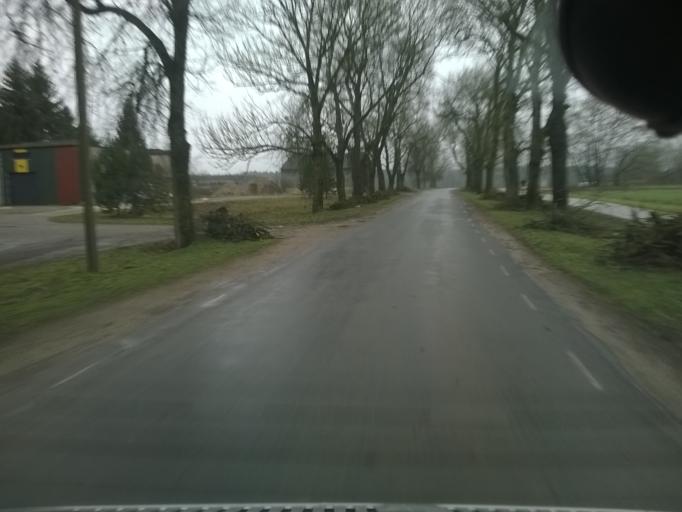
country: EE
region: Harju
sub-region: Nissi vald
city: Riisipere
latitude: 59.1282
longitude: 24.4725
